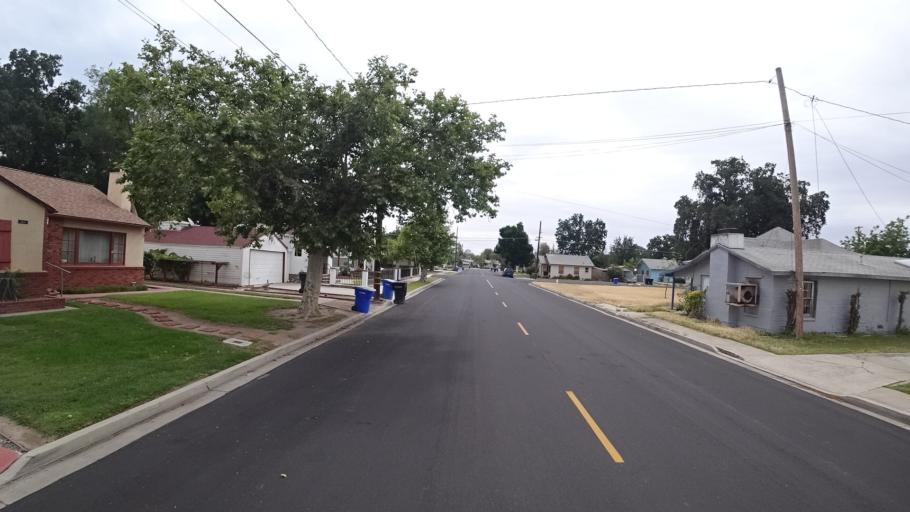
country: US
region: California
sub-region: Kings County
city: Hanford
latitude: 36.3408
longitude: -119.6512
